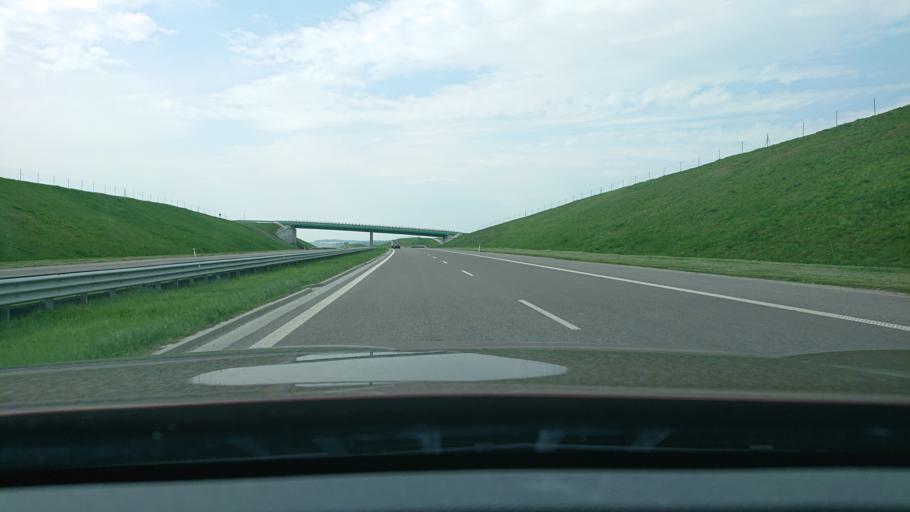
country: PL
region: Subcarpathian Voivodeship
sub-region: Powiat jaroslawski
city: Ostrow
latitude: 49.9295
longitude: 22.7186
